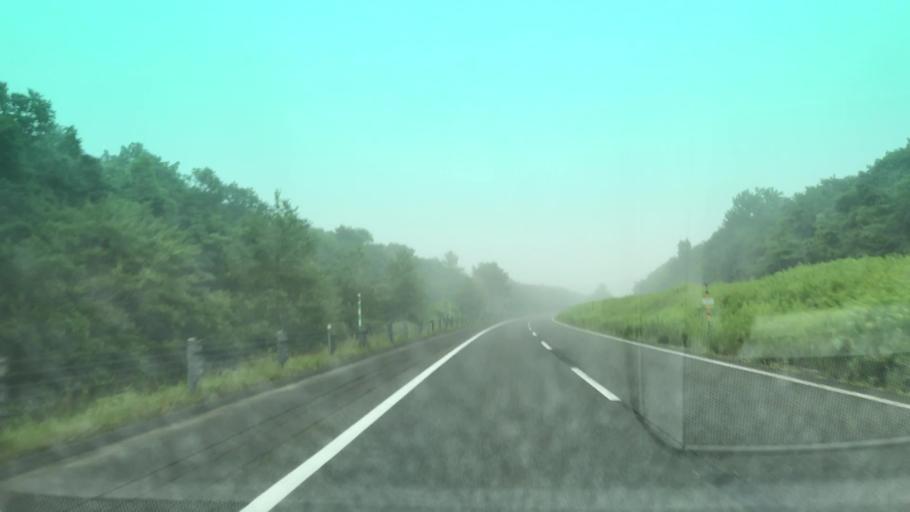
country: JP
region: Hokkaido
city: Chitose
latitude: 42.7968
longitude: 141.6268
